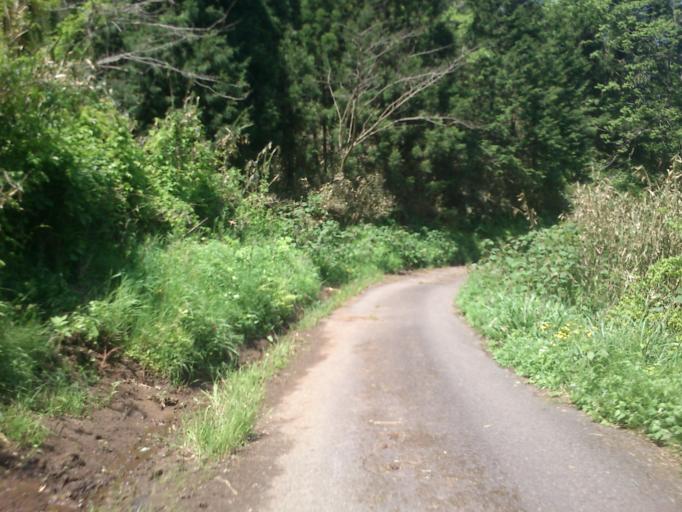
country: JP
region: Kyoto
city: Miyazu
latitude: 35.7128
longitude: 135.1433
